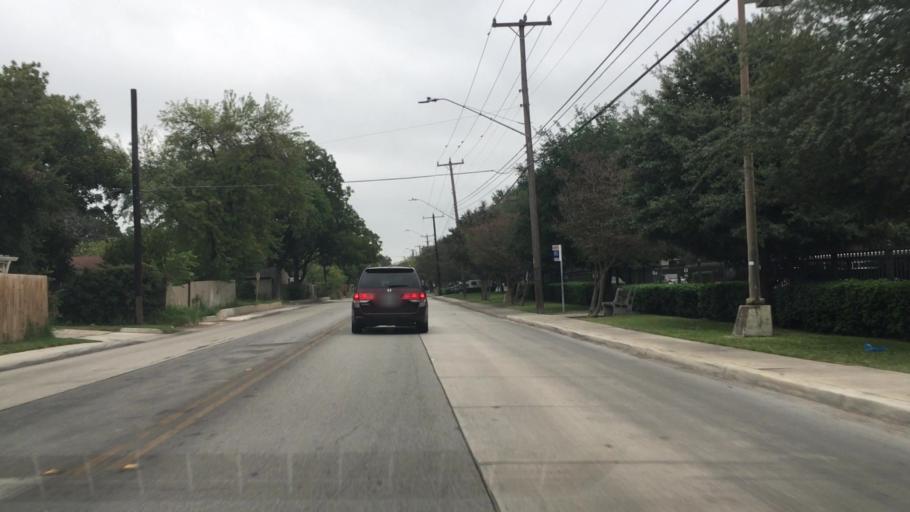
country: US
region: Texas
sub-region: Bexar County
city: Balcones Heights
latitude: 29.4790
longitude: -98.5516
